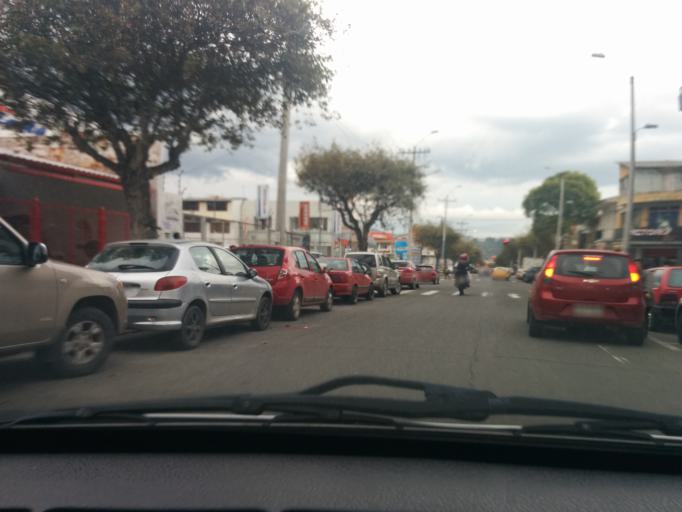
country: EC
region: Azuay
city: Cuenca
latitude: -2.8981
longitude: -78.9951
